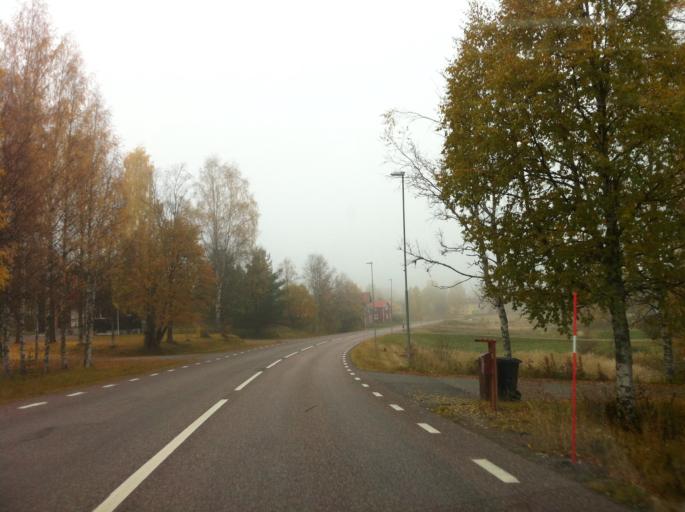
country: NO
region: Hedmark
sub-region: Trysil
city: Innbygda
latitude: 61.6899
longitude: 13.1566
